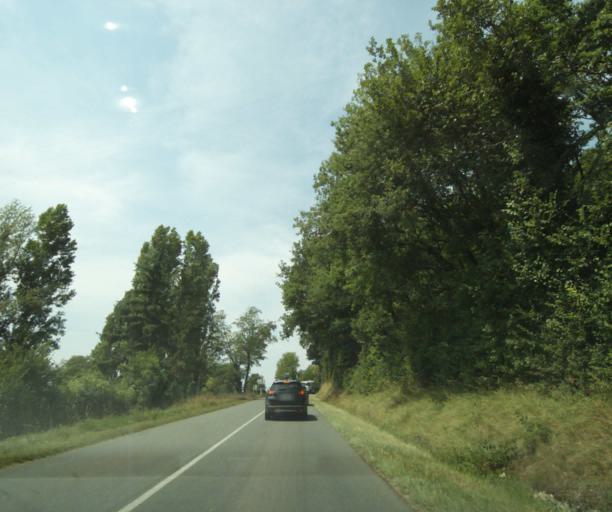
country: FR
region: Poitou-Charentes
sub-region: Departement de la Vienne
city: Lussac-les-Chateaux
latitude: 46.4085
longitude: 0.7058
